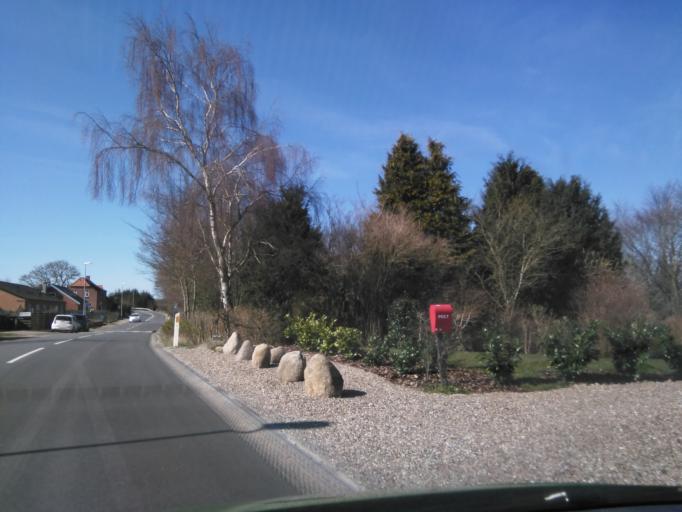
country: DK
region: Central Jutland
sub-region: Skanderborg Kommune
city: Ry
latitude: 56.0248
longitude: 9.7603
